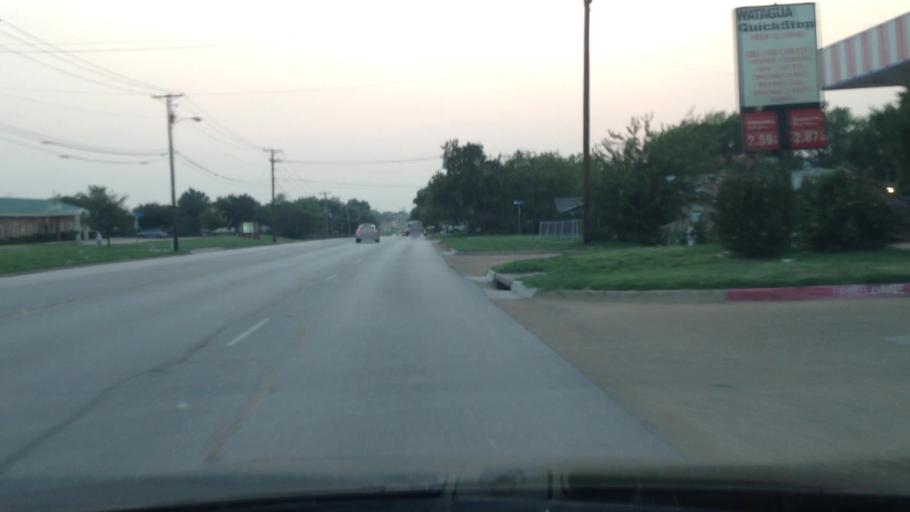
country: US
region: Texas
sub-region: Tarrant County
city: Watauga
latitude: 32.8605
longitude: -97.2419
